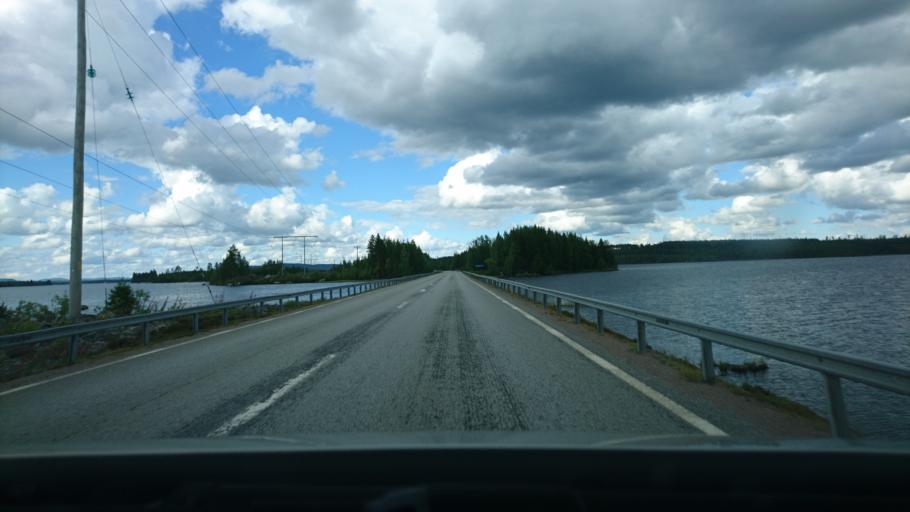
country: SE
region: Vaesterbotten
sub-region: Asele Kommun
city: Asele
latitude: 63.8920
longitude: 17.2166
